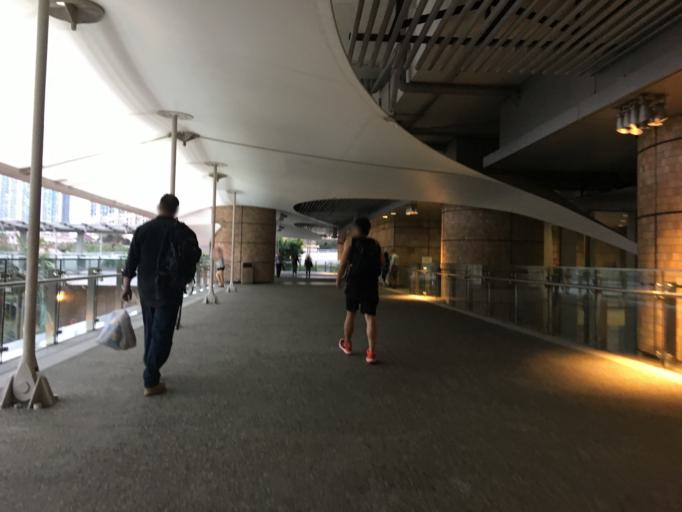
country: HK
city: Tai O
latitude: 22.2915
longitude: 113.9465
